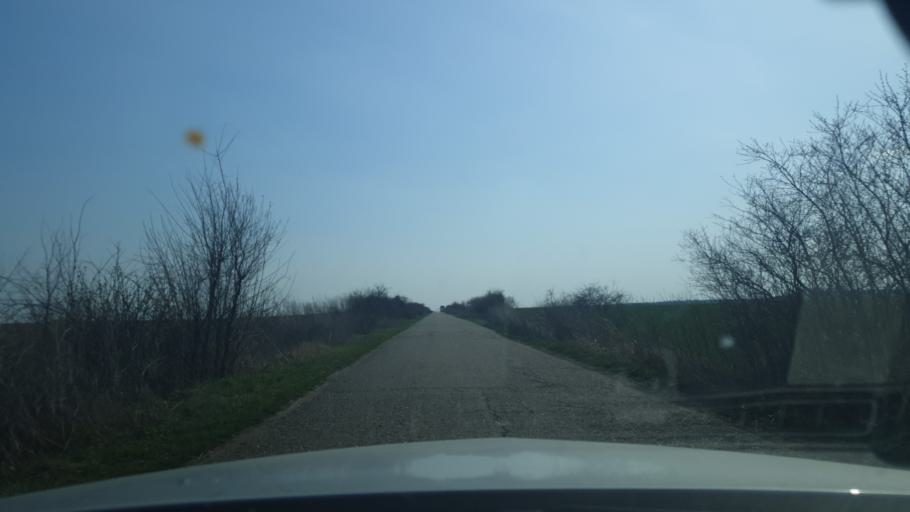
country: RS
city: Putinci
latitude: 45.0198
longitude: 19.9560
